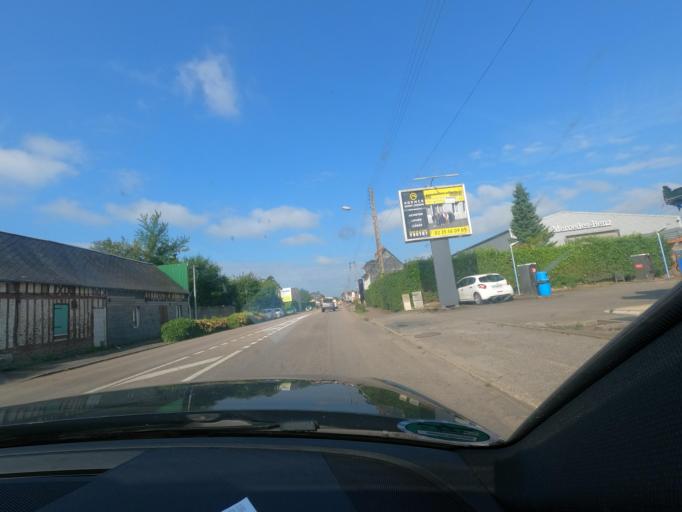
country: FR
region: Haute-Normandie
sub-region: Departement de la Seine-Maritime
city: Sainte-Marie-des-Champs
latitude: 49.6215
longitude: 0.7686
